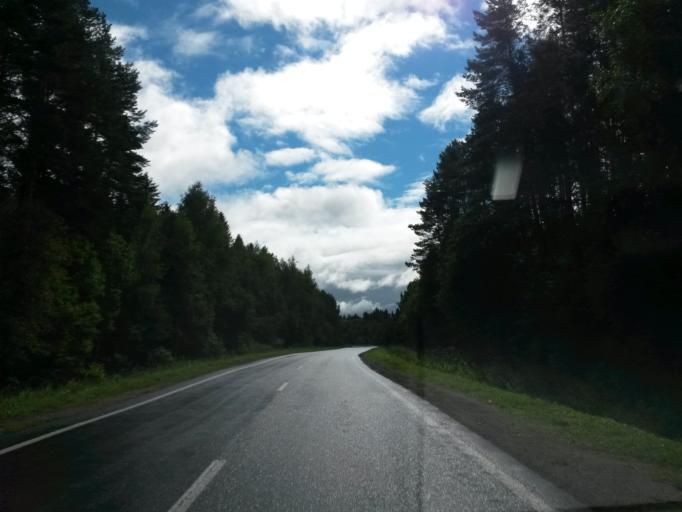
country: RU
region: Jaroslavl
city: Konstantinovskiy
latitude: 57.8248
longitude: 39.6796
